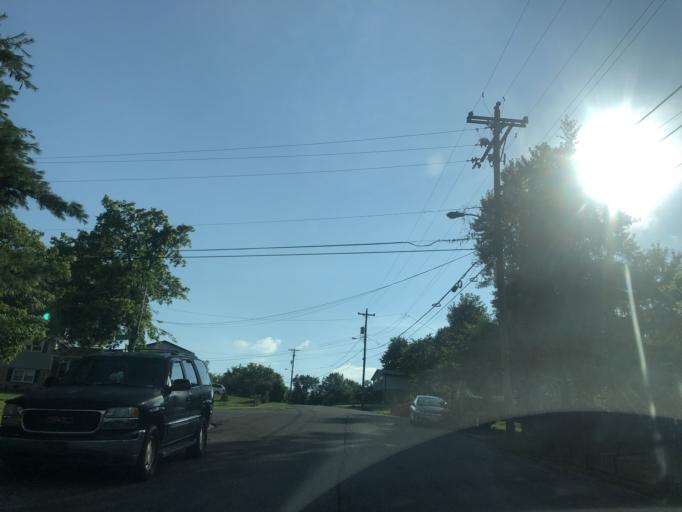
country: US
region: Tennessee
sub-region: Davidson County
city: Nashville
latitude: 36.2285
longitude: -86.8313
